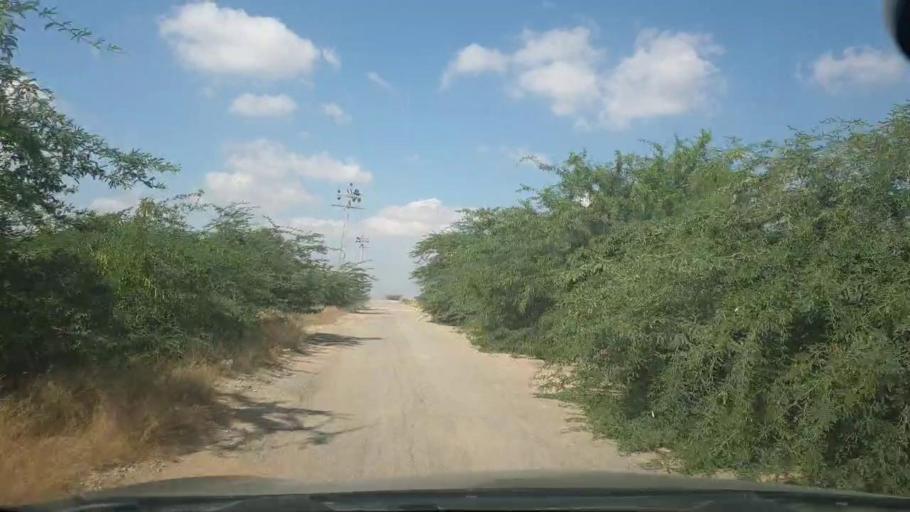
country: PK
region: Sindh
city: Malir Cantonment
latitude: 25.0630
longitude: 67.4088
